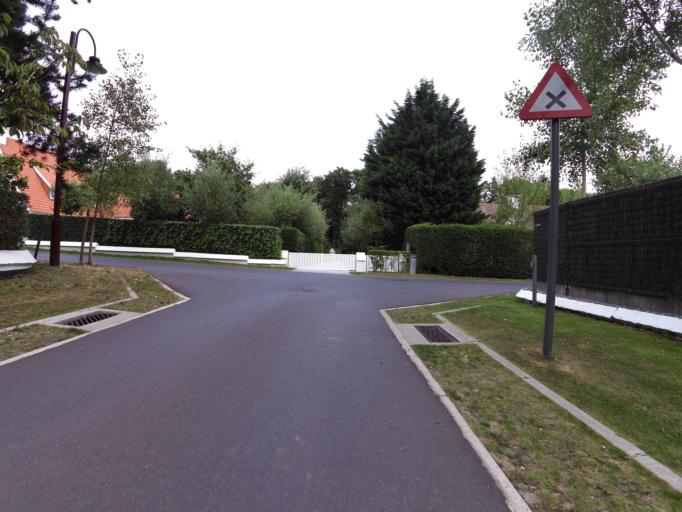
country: BE
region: Flanders
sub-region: Provincie West-Vlaanderen
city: De Haan
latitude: 51.2766
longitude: 3.0413
